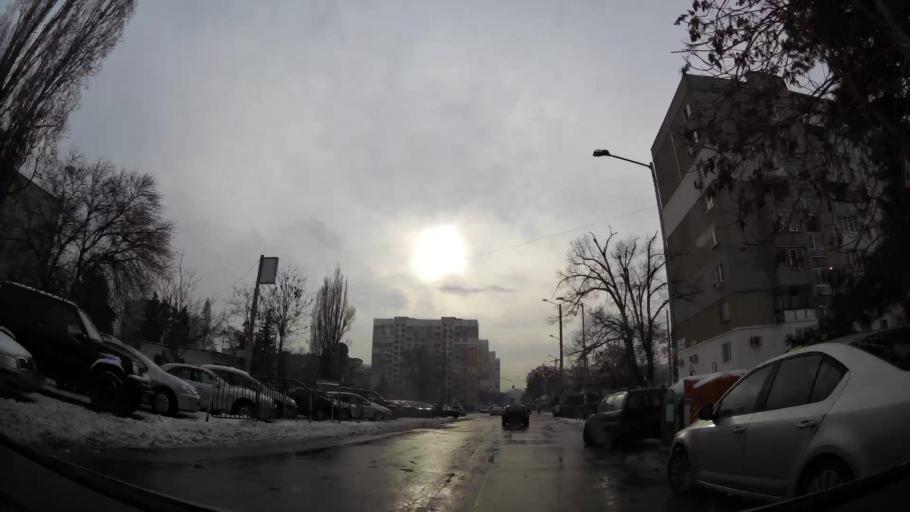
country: BG
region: Sofia-Capital
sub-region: Stolichna Obshtina
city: Sofia
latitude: 42.7147
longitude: 23.3067
